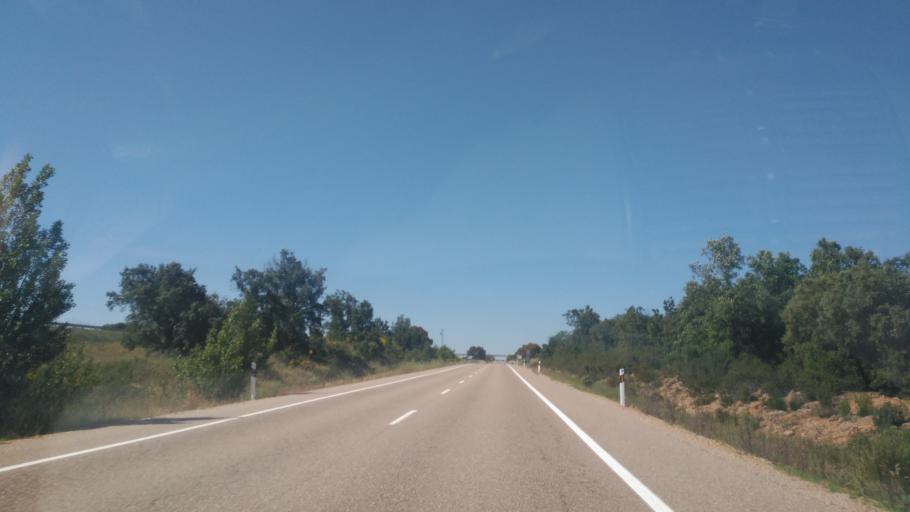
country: ES
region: Castille and Leon
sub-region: Provincia de Salamanca
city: Topas
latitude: 41.1517
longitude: -5.6952
